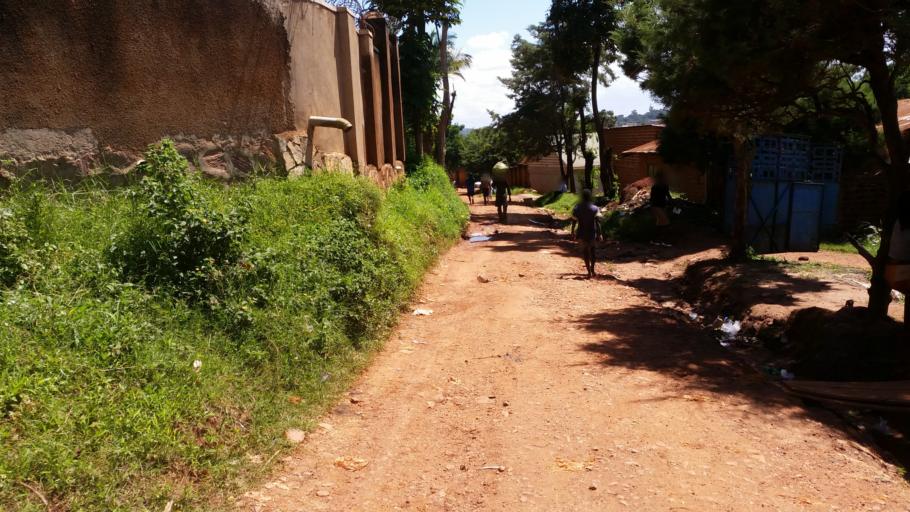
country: UG
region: Central Region
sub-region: Wakiso District
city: Kireka
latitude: 0.3422
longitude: 32.6486
